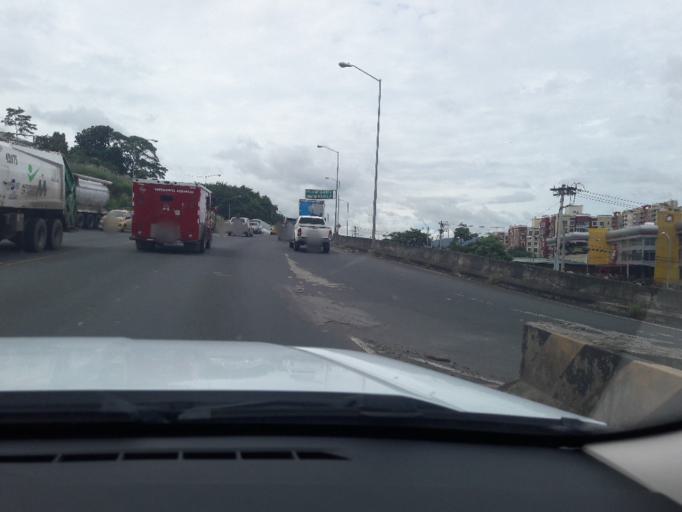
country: PA
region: Panama
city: Panama
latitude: 9.0227
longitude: -79.5264
